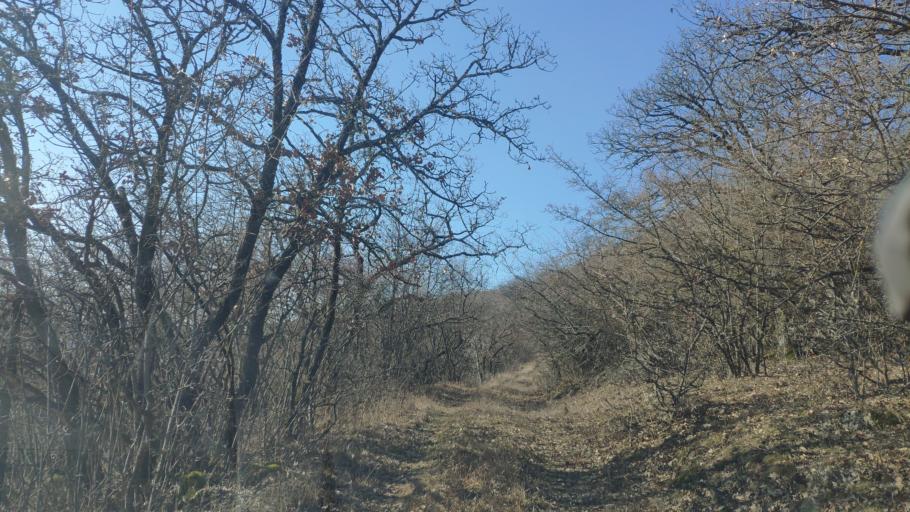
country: SK
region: Kosicky
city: Roznava
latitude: 48.6035
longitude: 20.7187
